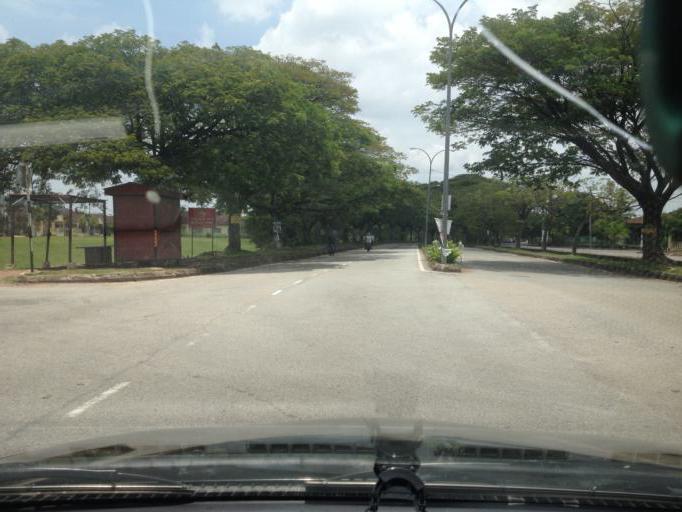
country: MY
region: Kedah
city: Sungai Petani
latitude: 5.6049
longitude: 100.5428
